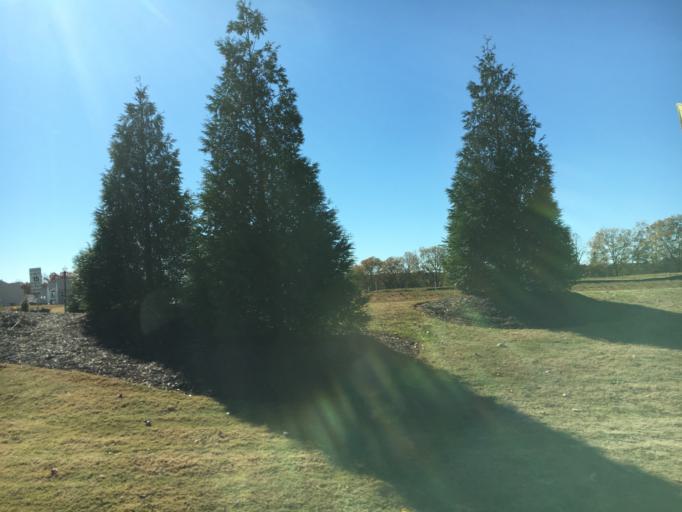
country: US
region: South Carolina
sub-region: Spartanburg County
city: Duncan
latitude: 34.8957
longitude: -82.1257
